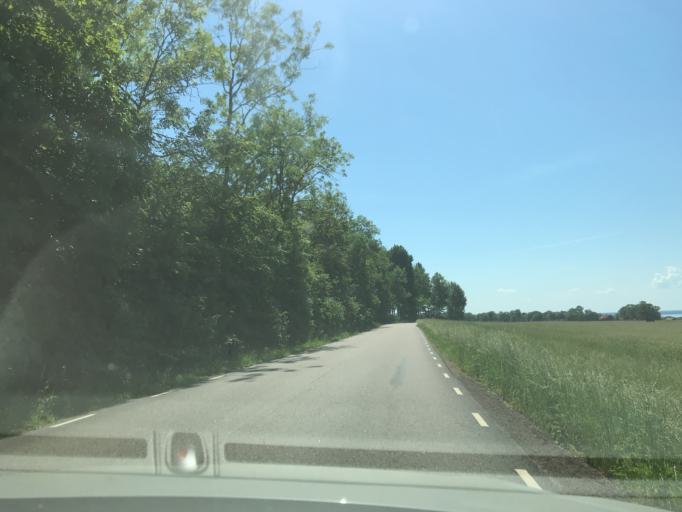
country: SE
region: Vaestra Goetaland
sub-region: Gotene Kommun
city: Kallby
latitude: 58.5533
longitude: 13.3458
